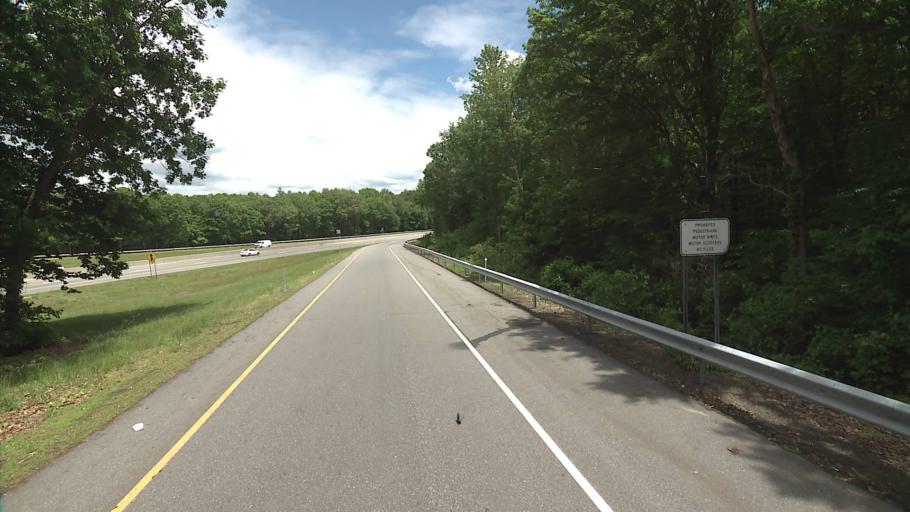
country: US
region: Connecticut
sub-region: Middlesex County
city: Clinton
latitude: 41.2936
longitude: -72.4877
